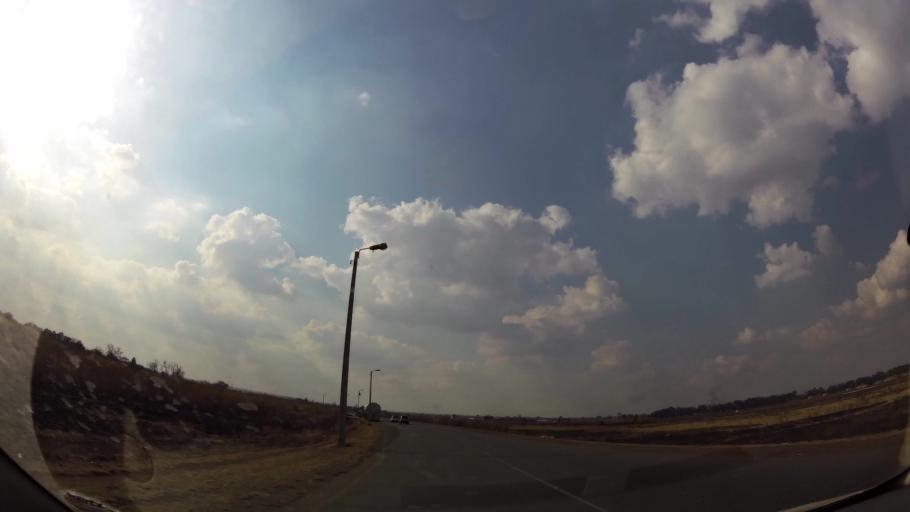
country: ZA
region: Gauteng
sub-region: Ekurhuleni Metropolitan Municipality
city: Germiston
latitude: -26.3004
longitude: 28.2129
